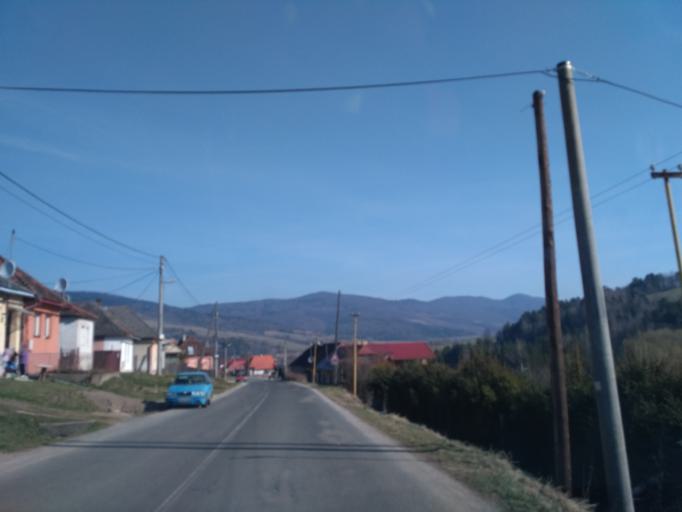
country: SK
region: Kosicky
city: Medzev
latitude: 48.7966
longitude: 20.8069
